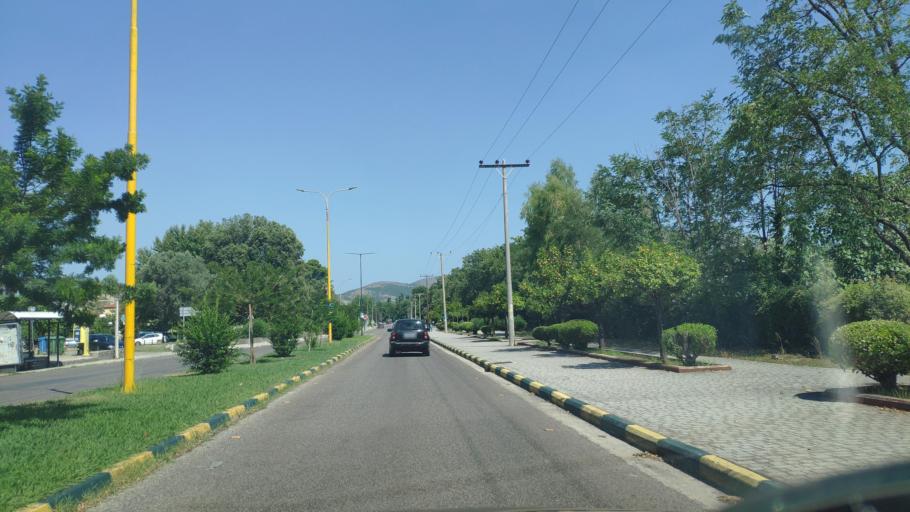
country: GR
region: Epirus
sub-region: Nomos Artas
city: Arta
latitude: 39.1636
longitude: 20.9917
